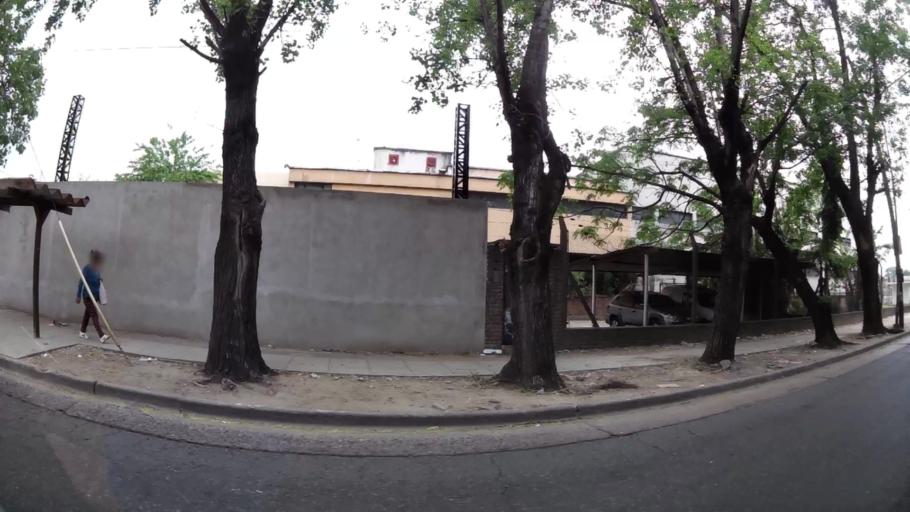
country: AR
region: Buenos Aires
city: San Justo
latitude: -34.6936
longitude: -58.5306
